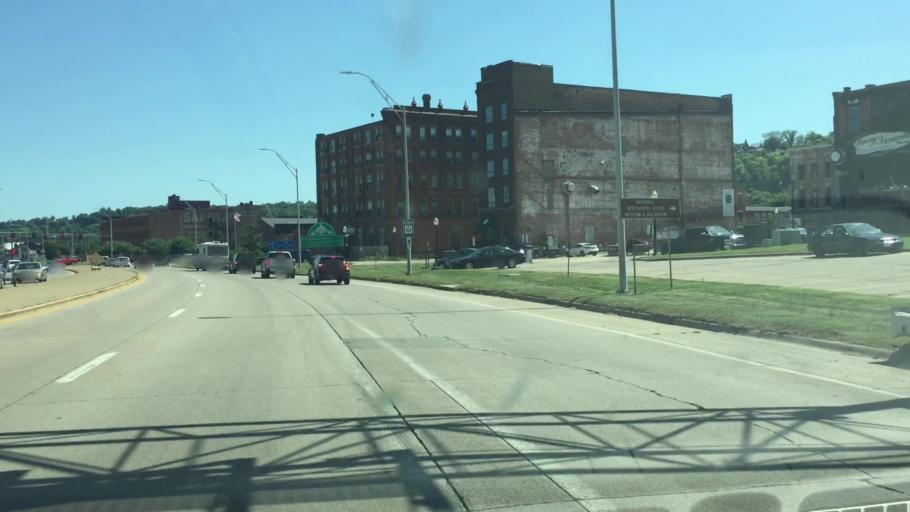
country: US
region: Iowa
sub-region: Dubuque County
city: Dubuque
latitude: 42.4962
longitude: -90.6633
